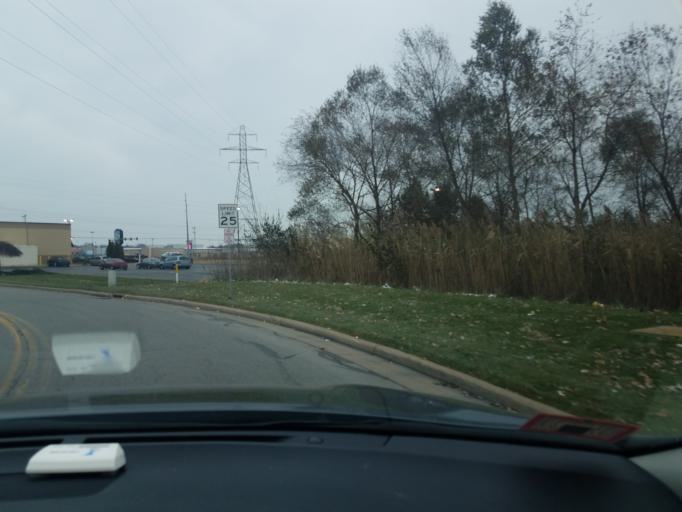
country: US
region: Ohio
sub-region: Erie County
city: Sandusky
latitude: 41.4036
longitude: -82.6615
